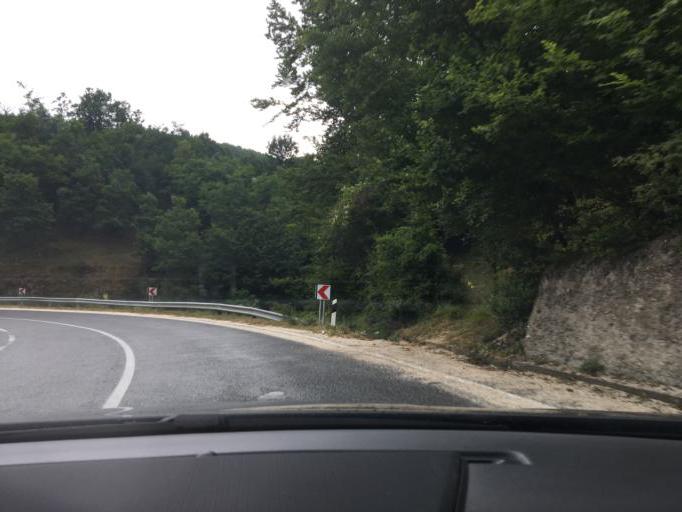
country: MK
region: Kriva Palanka
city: Kriva Palanka
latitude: 42.2232
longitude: 22.4268
